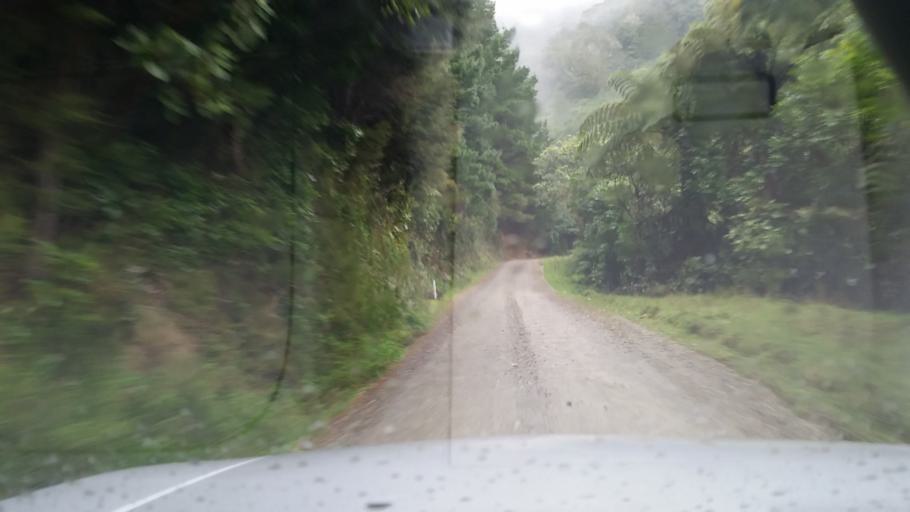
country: NZ
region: Marlborough
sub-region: Marlborough District
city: Picton
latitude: -41.1426
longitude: 174.0479
